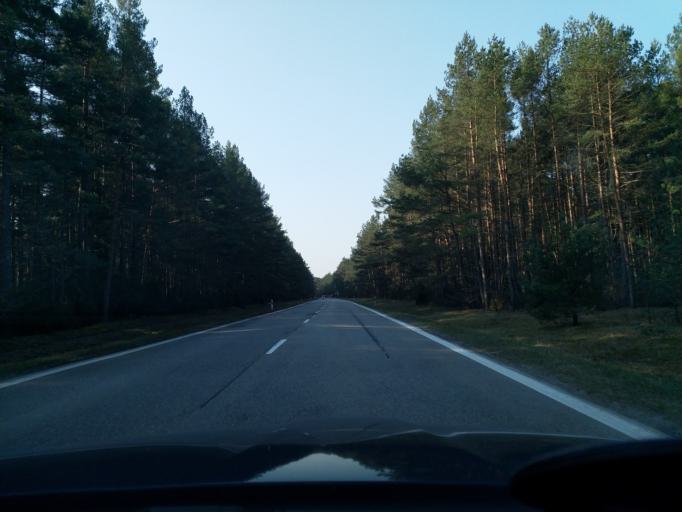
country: LT
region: Klaipedos apskritis
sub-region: Palanga
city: Sventoji
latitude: 56.0277
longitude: 21.1164
